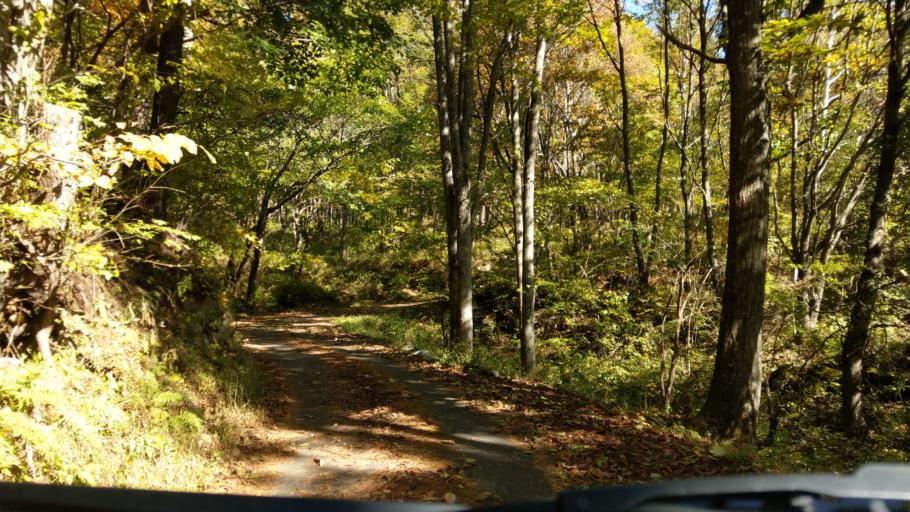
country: JP
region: Nagano
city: Komoro
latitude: 36.3806
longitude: 138.4297
